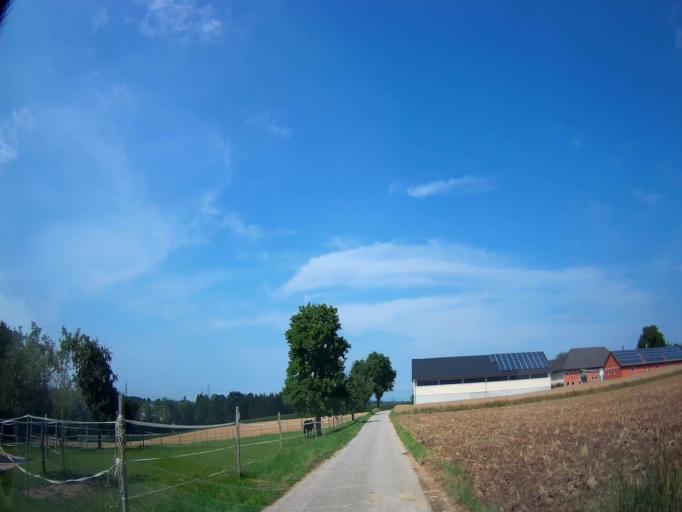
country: AT
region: Upper Austria
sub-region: Politischer Bezirk Kirchdorf an der Krems
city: Kremsmunster
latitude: 48.0797
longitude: 14.0999
